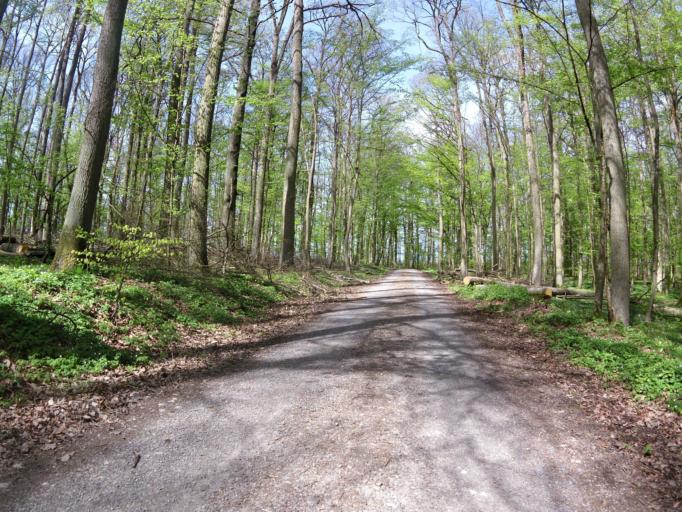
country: DE
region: Bavaria
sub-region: Regierungsbezirk Unterfranken
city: Rimpar
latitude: 49.8678
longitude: 9.9831
